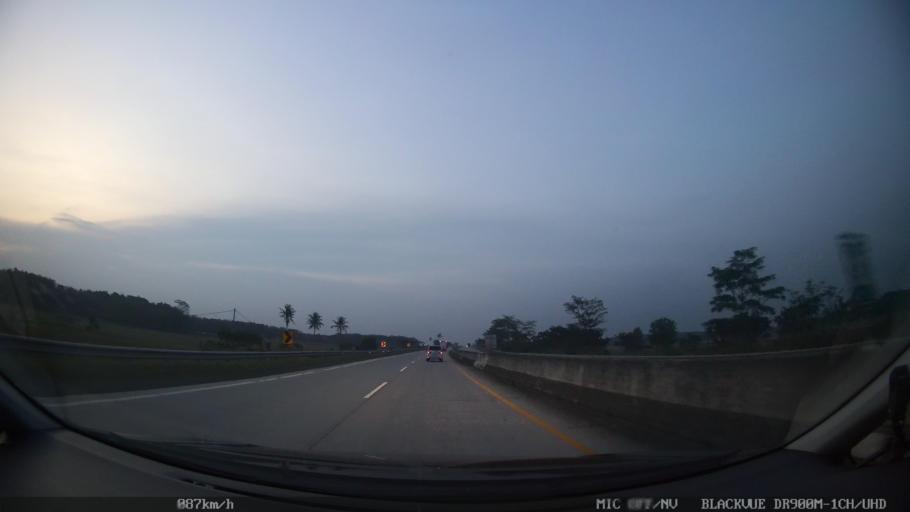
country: ID
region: Lampung
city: Sidorejo
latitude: -5.5897
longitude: 105.5466
